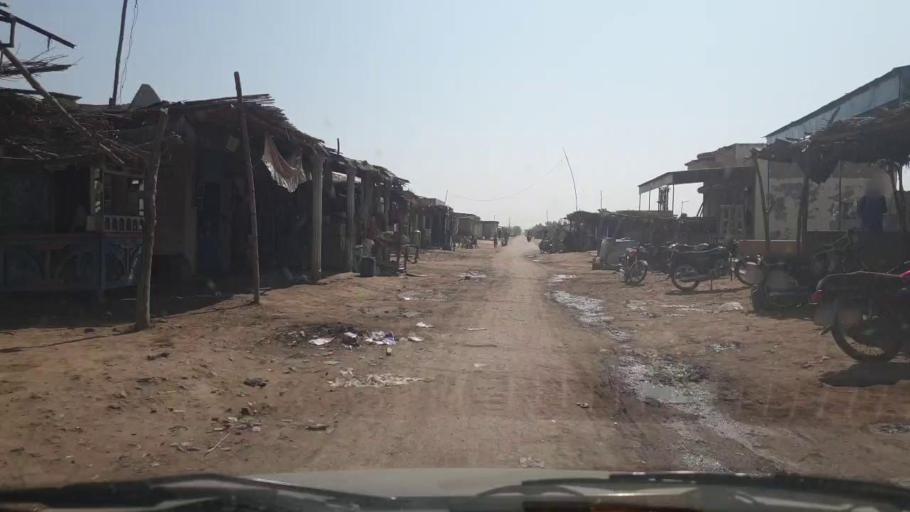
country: PK
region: Sindh
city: Samaro
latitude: 25.2766
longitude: 69.3416
